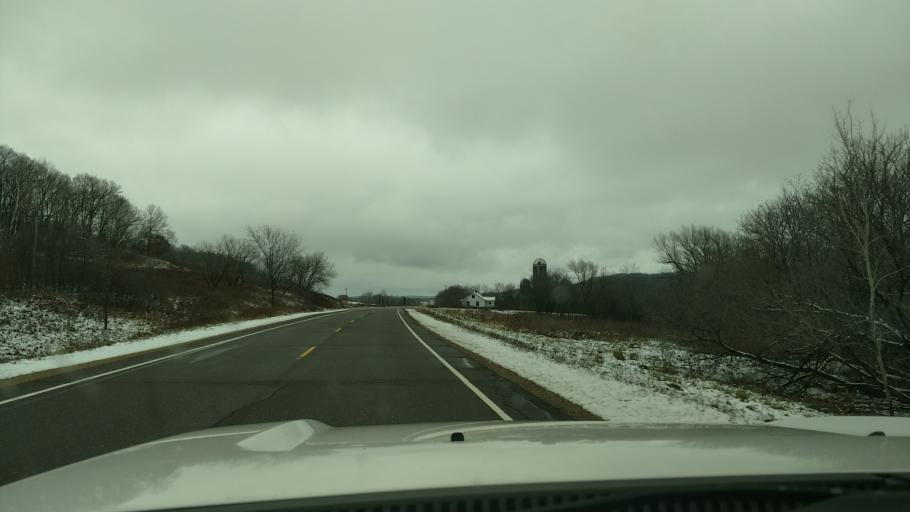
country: US
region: Wisconsin
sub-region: Dunn County
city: Tainter Lake
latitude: 45.1367
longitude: -91.7990
